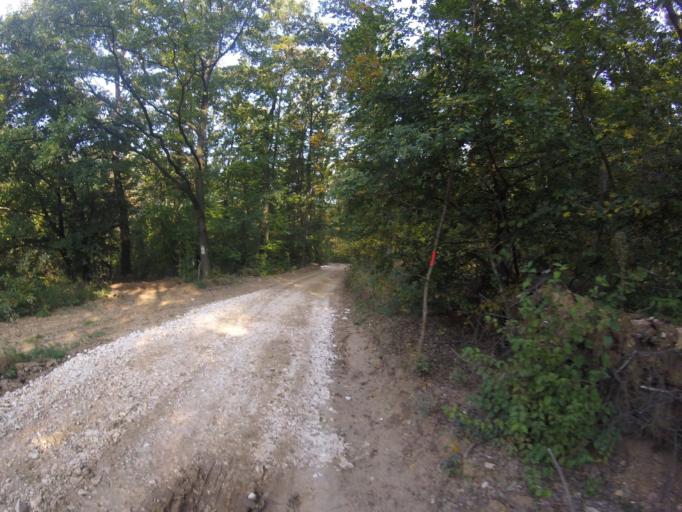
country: HU
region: Komarom-Esztergom
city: Piliscsev
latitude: 47.6850
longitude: 18.8544
